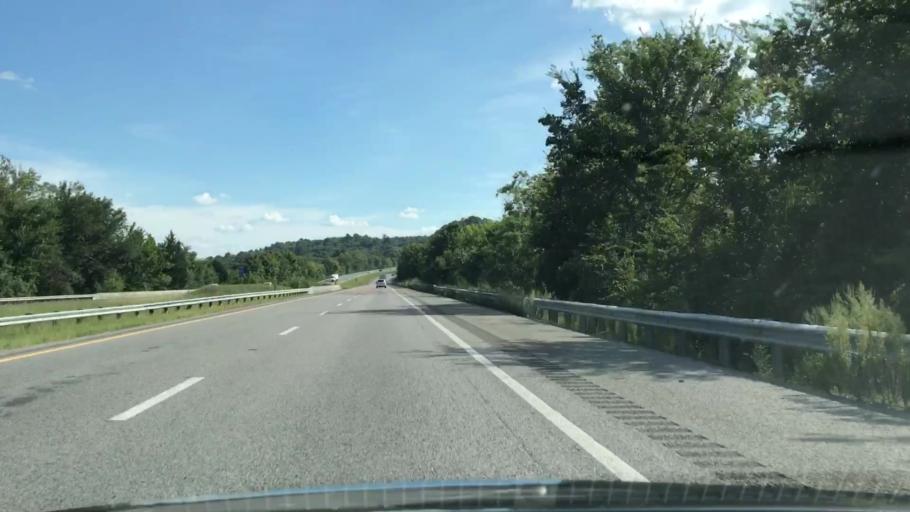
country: US
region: Alabama
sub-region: Limestone County
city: Ardmore
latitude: 35.1314
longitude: -86.8778
